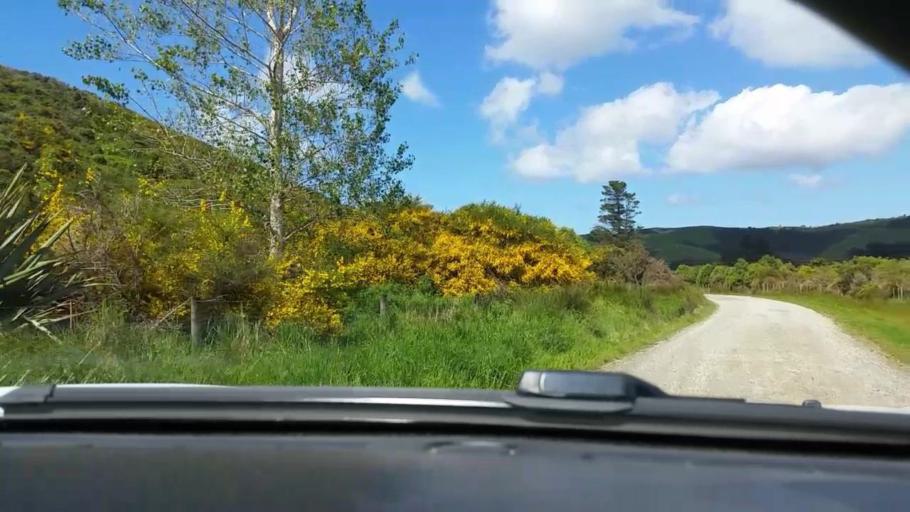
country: NZ
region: Otago
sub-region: Clutha District
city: Papatowai
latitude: -46.5955
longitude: 169.1344
